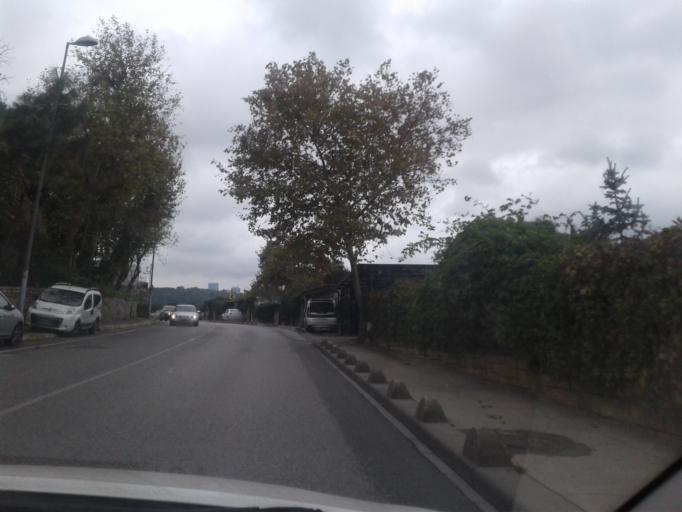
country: TR
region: Istanbul
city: UEskuedar
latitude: 41.0740
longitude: 29.0575
